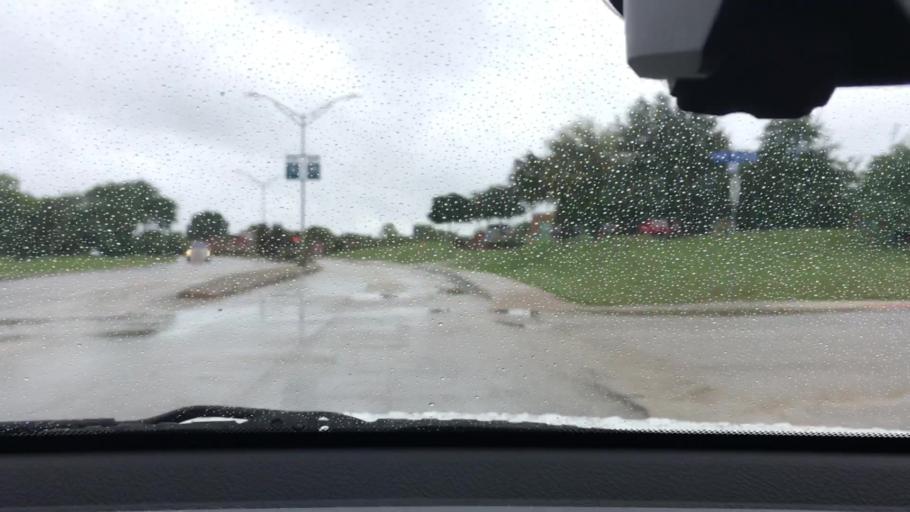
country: US
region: Texas
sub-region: Bexar County
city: Leon Valley
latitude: 29.5251
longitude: -98.5909
